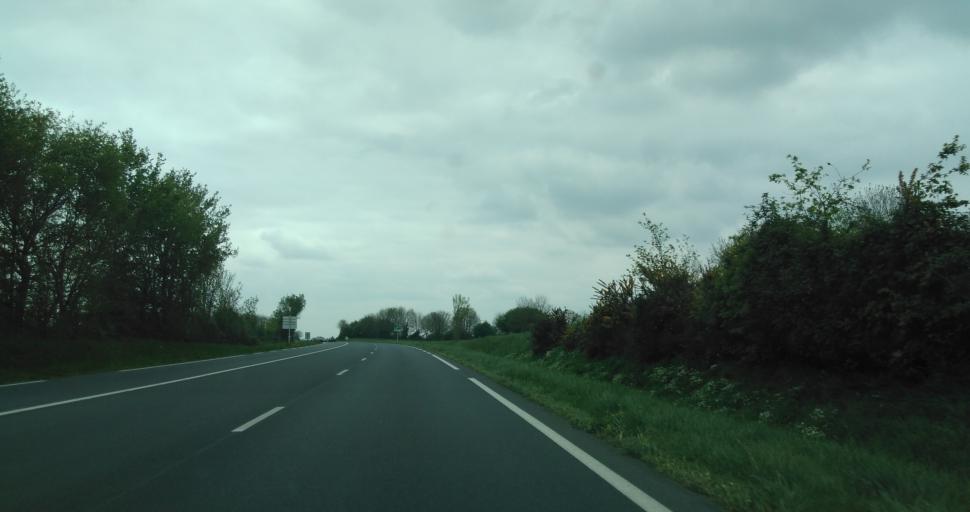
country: FR
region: Poitou-Charentes
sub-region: Departement des Deux-Sevres
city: Champdeniers-Saint-Denis
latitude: 46.4423
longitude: -0.3905
